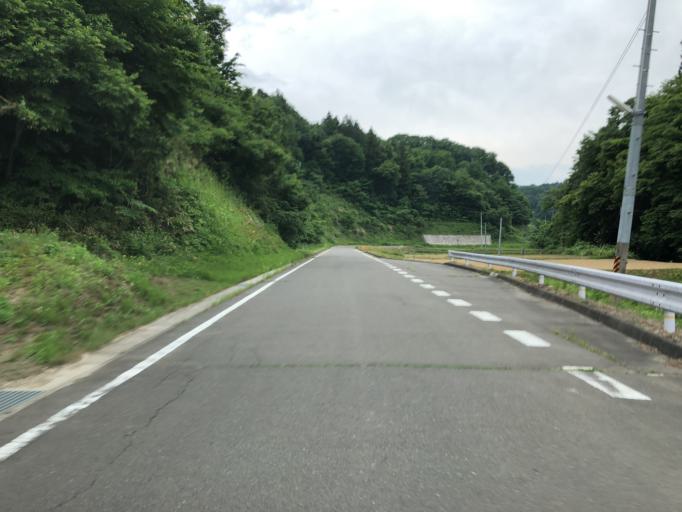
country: JP
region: Fukushima
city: Funehikimachi-funehiki
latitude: 37.4533
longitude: 140.5291
